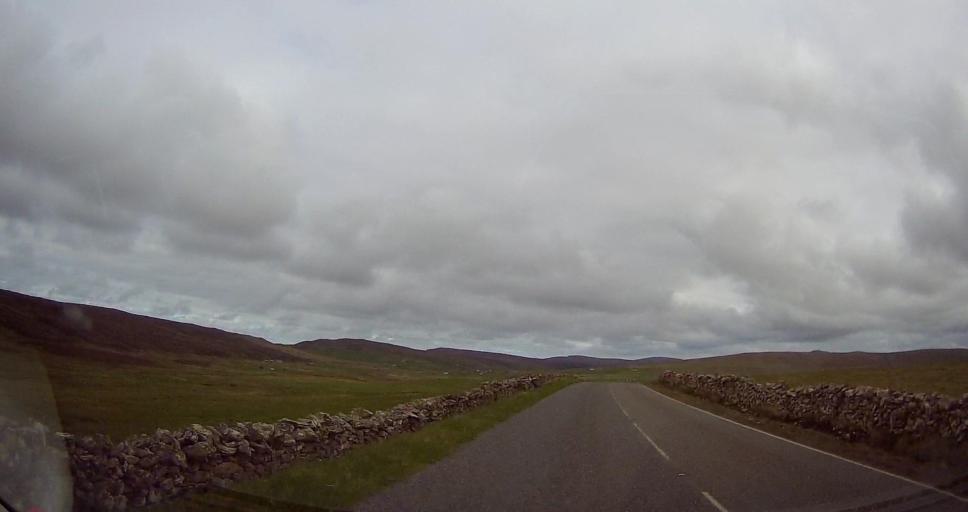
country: GB
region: Scotland
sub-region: Shetland Islands
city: Shetland
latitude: 60.7478
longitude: -0.8850
